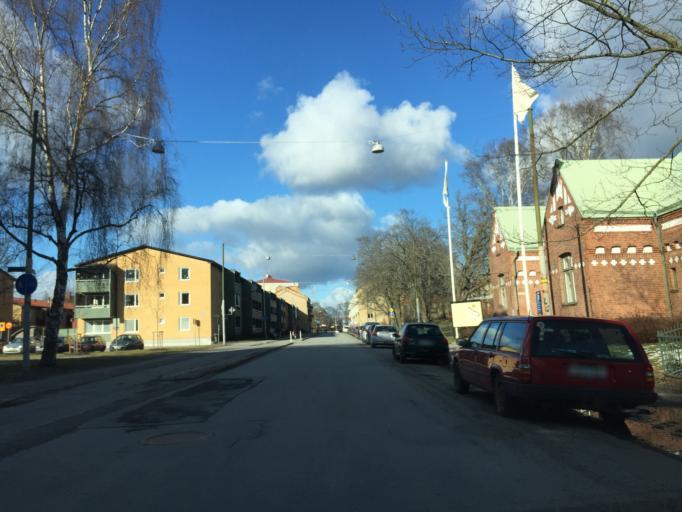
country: SE
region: OErebro
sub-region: Orebro Kommun
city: Orebro
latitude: 59.2793
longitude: 15.2224
